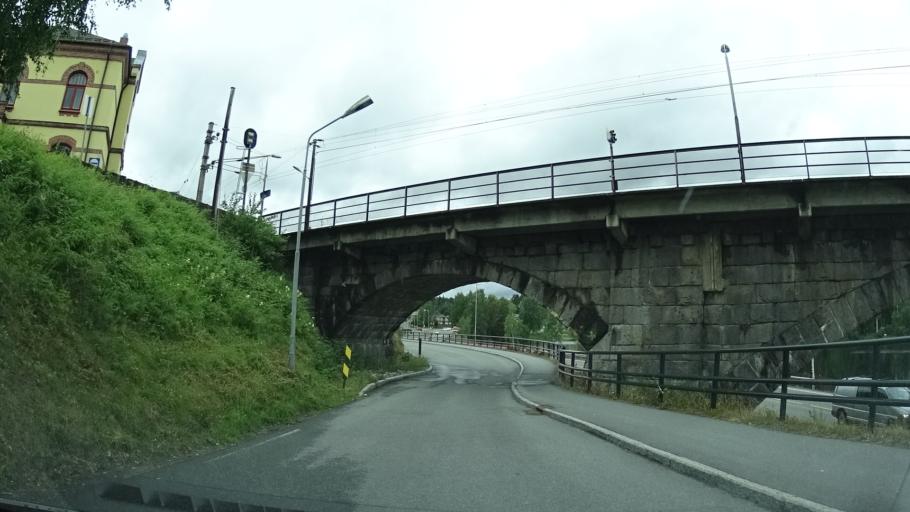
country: NO
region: Buskerud
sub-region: Ringerike
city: Honefoss
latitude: 60.1694
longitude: 10.2502
